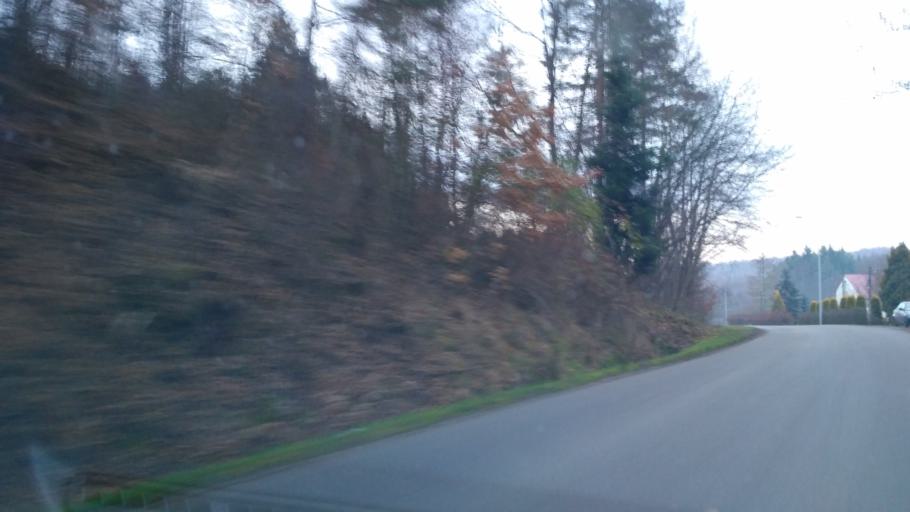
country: PL
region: Subcarpathian Voivodeship
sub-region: Powiat strzyzowski
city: Niebylec
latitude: 49.8604
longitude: 21.8931
